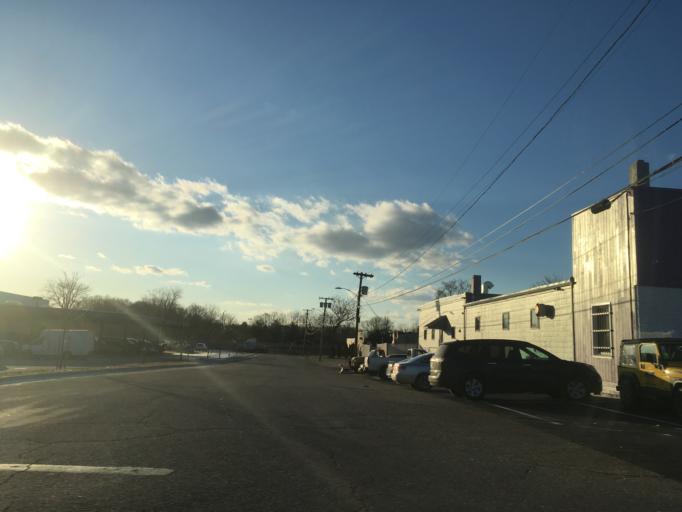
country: US
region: Rhode Island
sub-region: Providence County
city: Cranston
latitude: 41.7957
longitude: -71.4390
